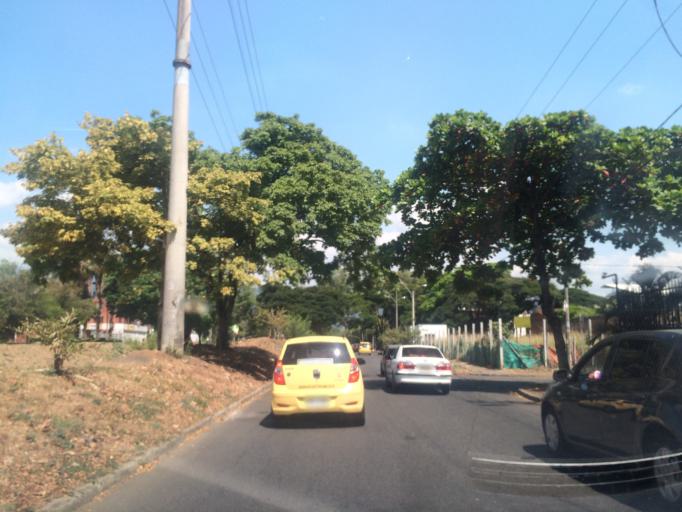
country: CO
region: Valle del Cauca
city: Cali
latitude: 3.4070
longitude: -76.5283
